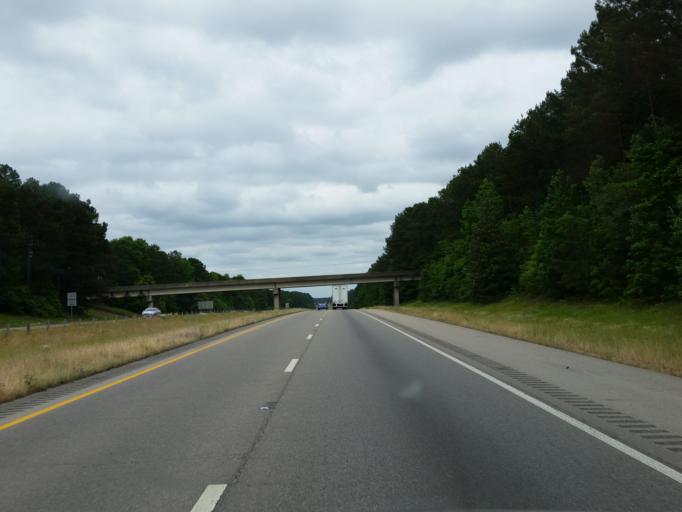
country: US
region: Alabama
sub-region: Sumter County
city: York
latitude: 32.4446
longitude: -88.4171
